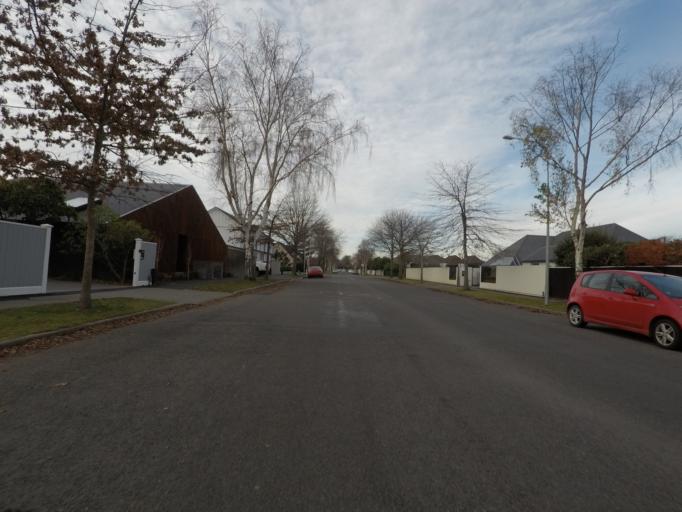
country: NZ
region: Canterbury
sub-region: Christchurch City
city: Christchurch
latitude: -43.5155
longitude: 172.6178
